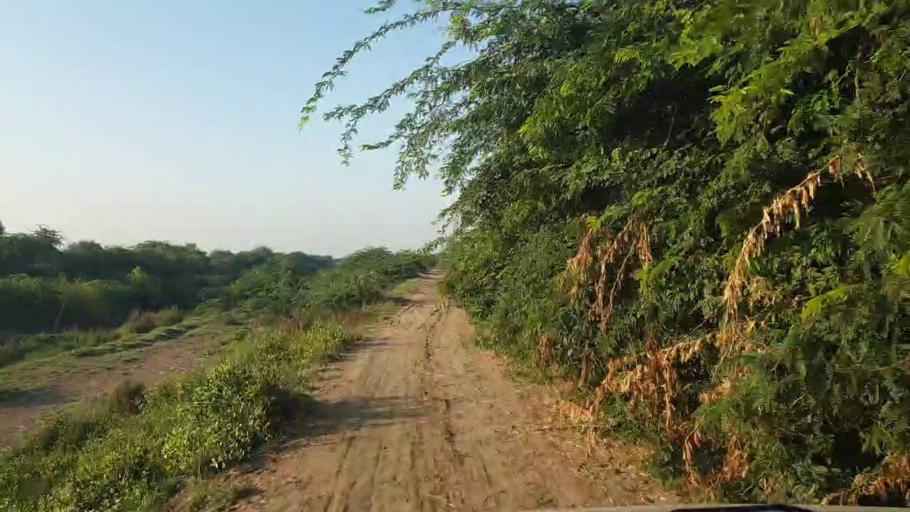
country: PK
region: Sindh
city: Badin
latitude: 24.6255
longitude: 68.7941
